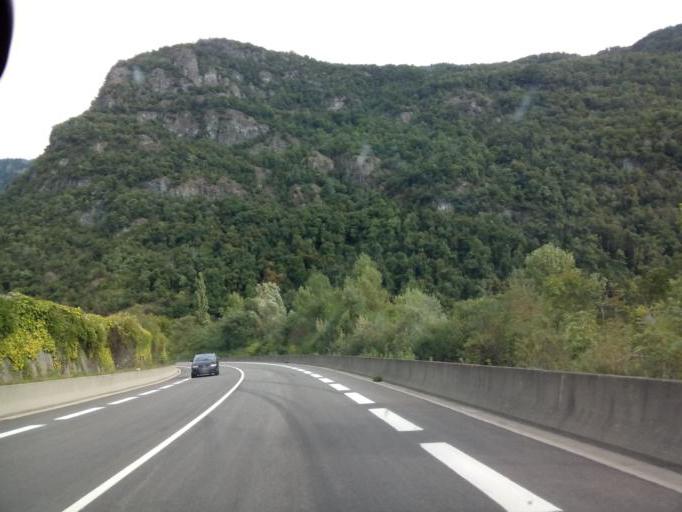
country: FR
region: Rhone-Alpes
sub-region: Departement de l'Isere
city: Vaulnaveys-le-Bas
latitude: 45.0520
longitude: 5.8323
